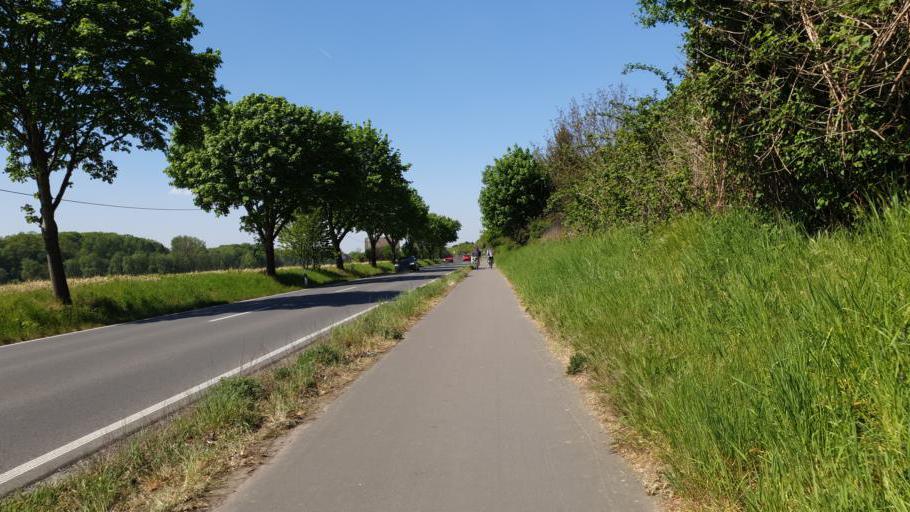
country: DE
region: North Rhine-Westphalia
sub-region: Regierungsbezirk Koln
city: Odenthal
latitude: 51.0305
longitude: 7.0695
